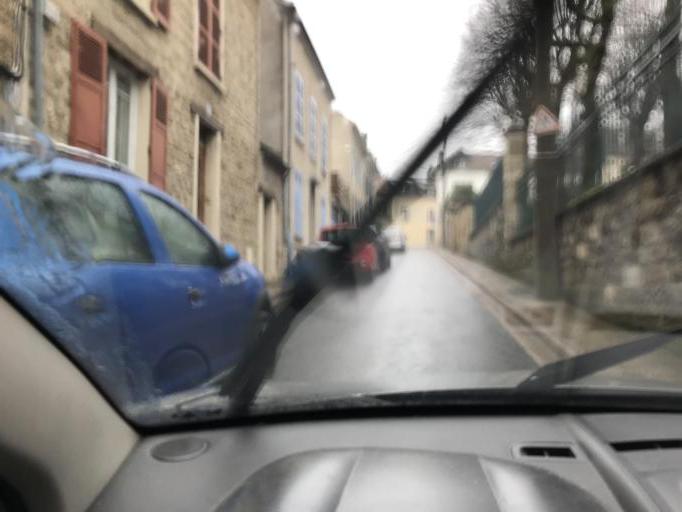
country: FR
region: Ile-de-France
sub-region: Departement du Val-d'Oise
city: Pontoise
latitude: 49.0509
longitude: 2.0926
